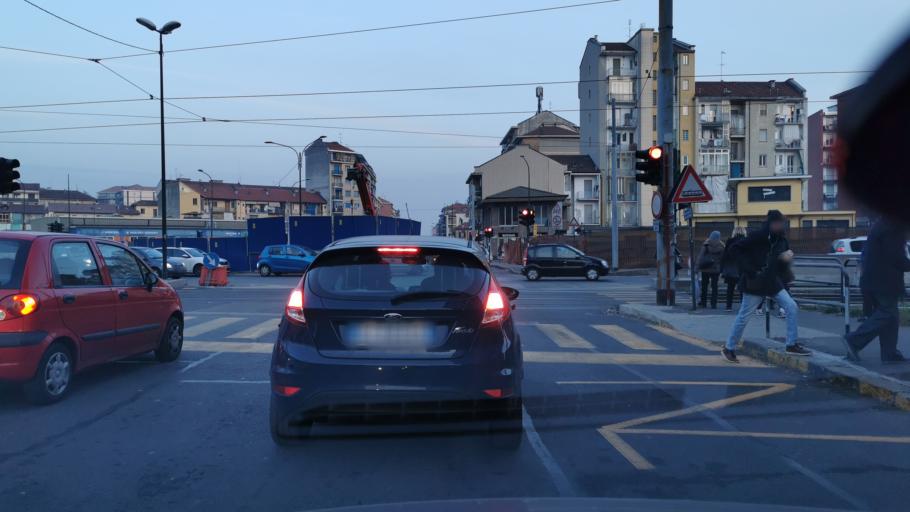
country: IT
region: Piedmont
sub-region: Provincia di Torino
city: Venaria Reale
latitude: 45.1035
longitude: 7.6617
